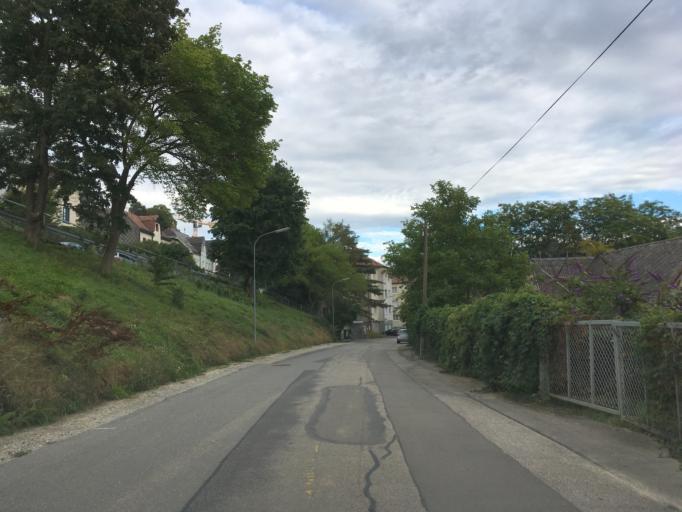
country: AT
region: Lower Austria
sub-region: Politischer Bezirk Tulln
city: Wordern
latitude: 48.3113
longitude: 16.2549
